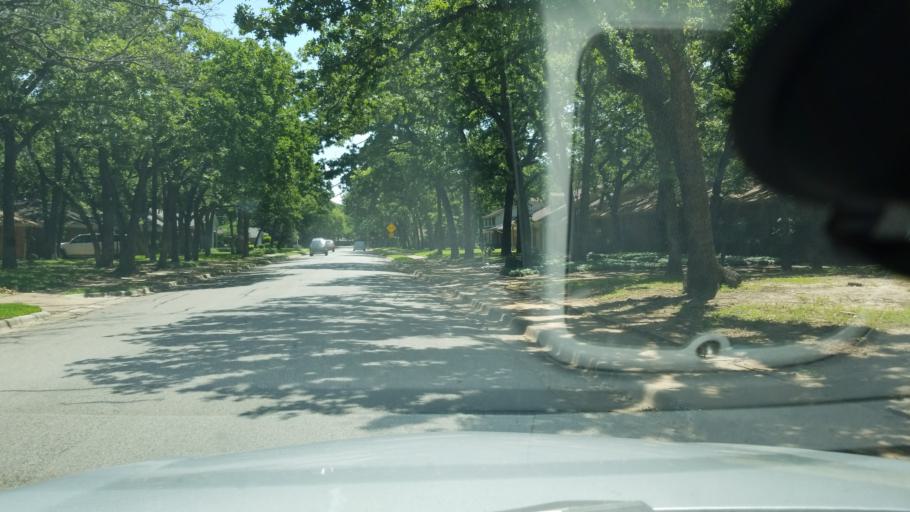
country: US
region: Texas
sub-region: Dallas County
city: Irving
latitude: 32.8338
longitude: -96.9572
